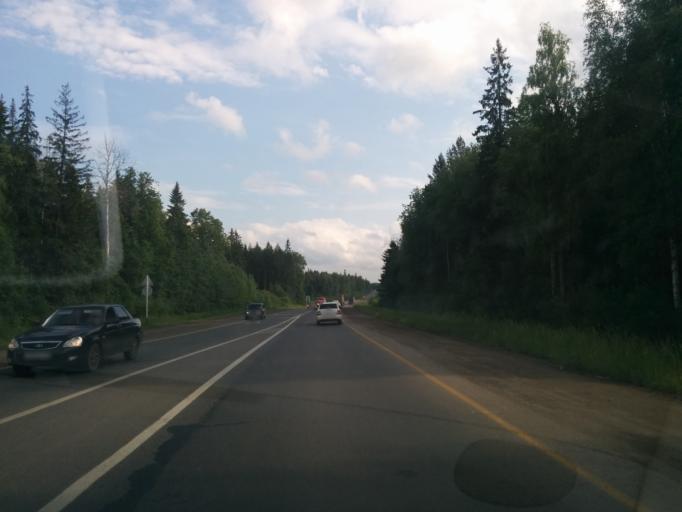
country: RU
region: Perm
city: Polazna
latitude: 58.1128
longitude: 56.4264
